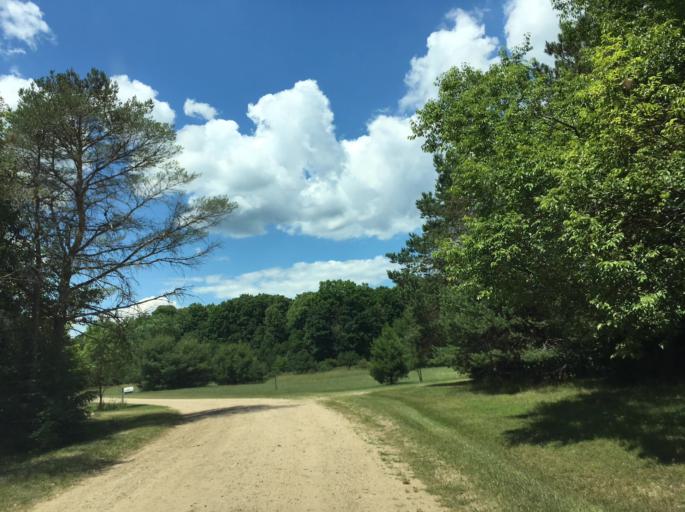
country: US
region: Michigan
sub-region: Osceola County
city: Evart
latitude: 43.8603
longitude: -85.3761
